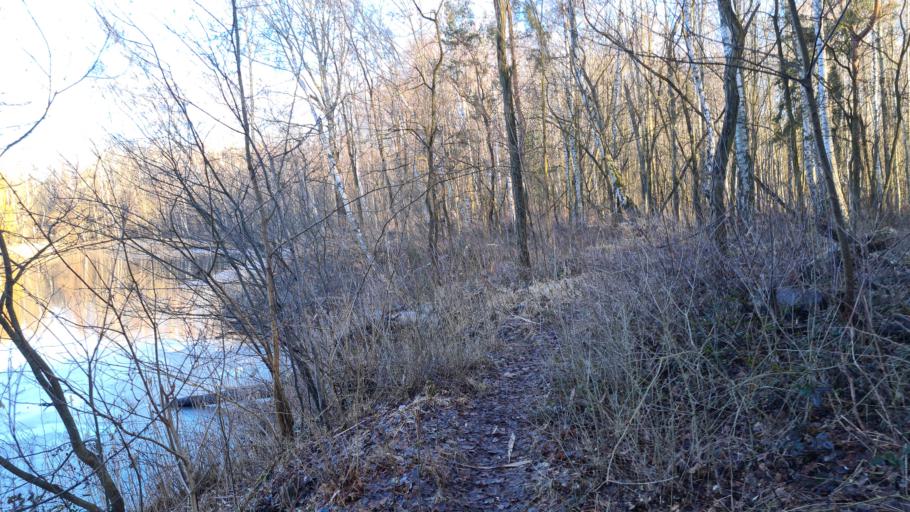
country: DE
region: Brandenburg
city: Trobitz
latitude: 51.5880
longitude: 13.4108
